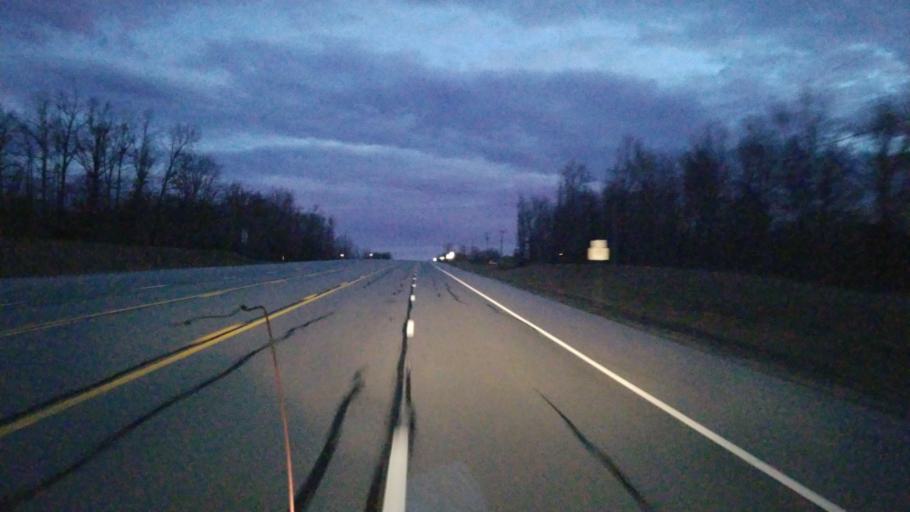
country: US
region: Tennessee
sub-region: Sequatchie County
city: Dunlap
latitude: 35.5280
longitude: -85.4691
